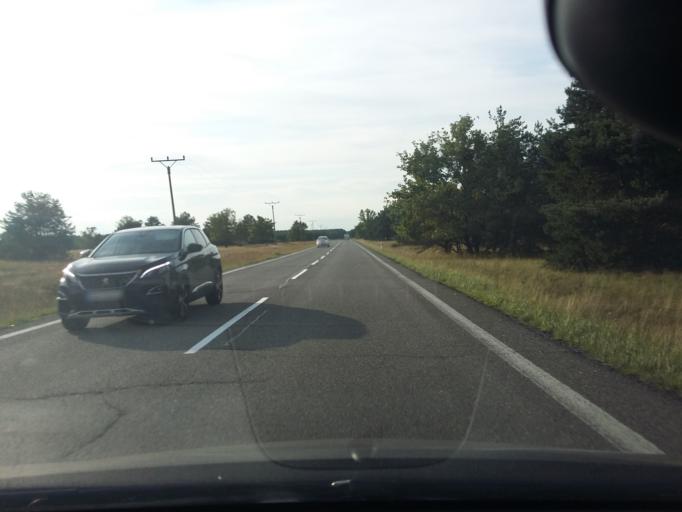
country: SK
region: Bratislavsky
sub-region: Okres Malacky
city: Malacky
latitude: 48.4143
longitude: 17.0642
